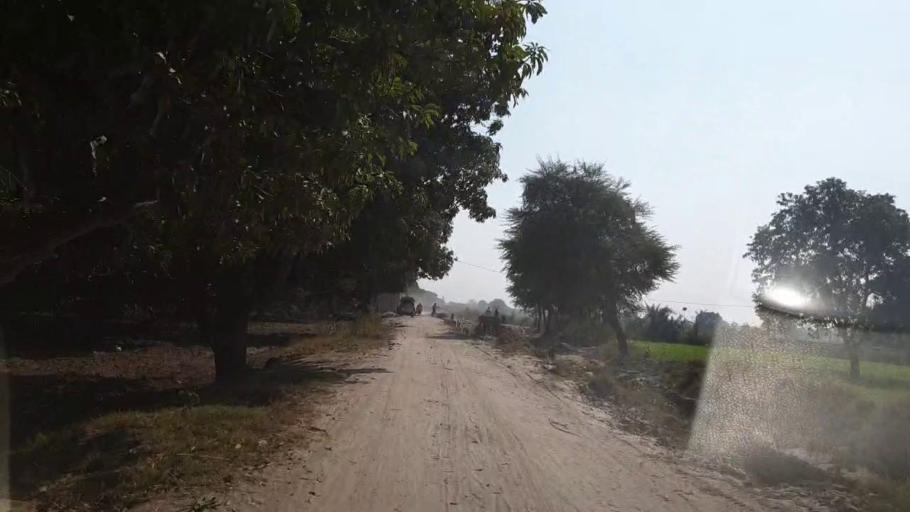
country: PK
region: Sindh
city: Matiari
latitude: 25.5127
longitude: 68.4607
